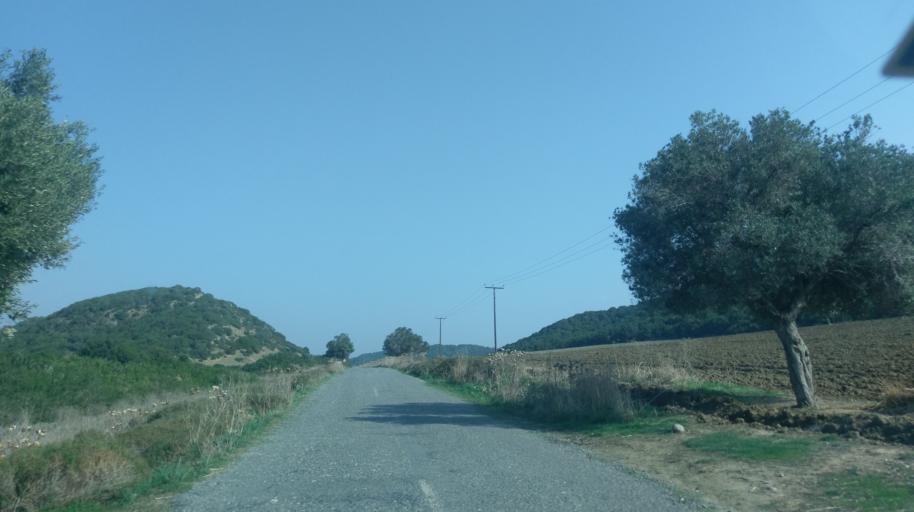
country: CY
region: Ammochostos
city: Rizokarpaso
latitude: 35.6326
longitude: 34.5000
